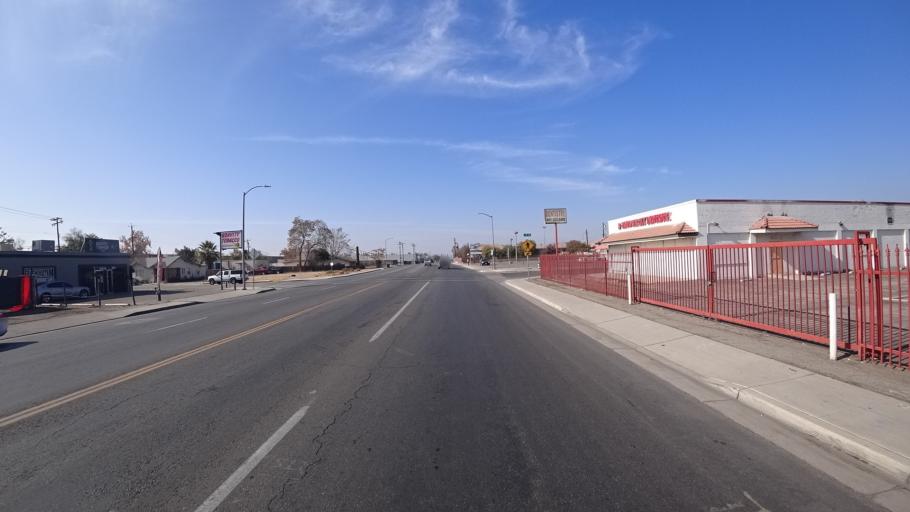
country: US
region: California
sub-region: Kern County
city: Bakersfield
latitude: 35.3540
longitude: -119.0081
